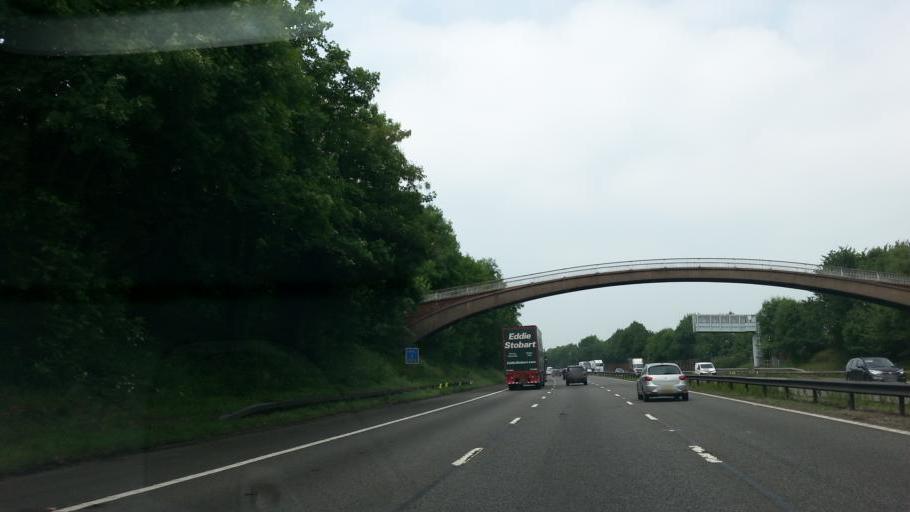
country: GB
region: England
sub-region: Staffordshire
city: Stafford
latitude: 52.7802
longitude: -2.1210
